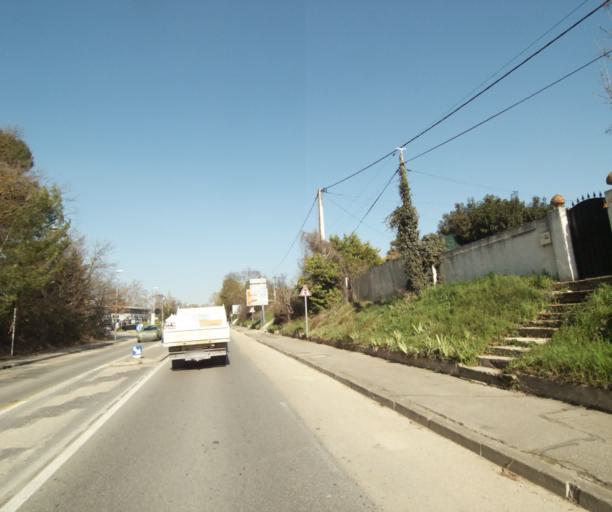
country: FR
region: Provence-Alpes-Cote d'Azur
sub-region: Departement des Bouches-du-Rhone
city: Bouc-Bel-Air
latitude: 43.4511
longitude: 5.3995
